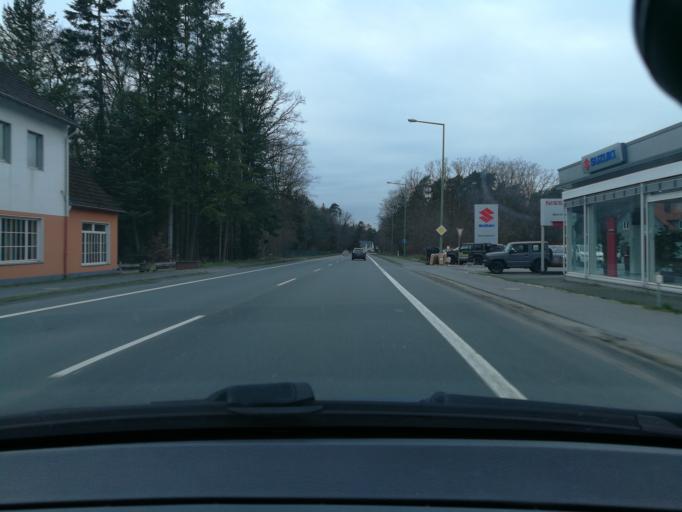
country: DE
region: North Rhine-Westphalia
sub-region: Regierungsbezirk Detmold
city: Oerlinghausen
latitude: 51.9348
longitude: 8.6000
